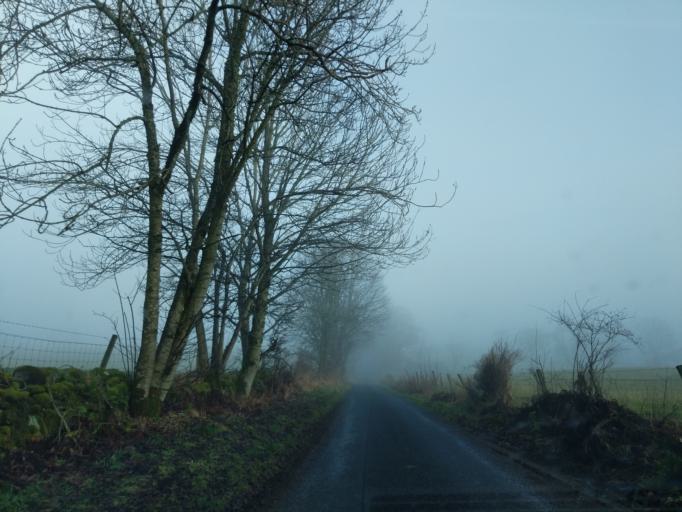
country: GB
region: Scotland
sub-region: Perth and Kinross
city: Auchterarder
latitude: 56.2816
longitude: -3.6940
